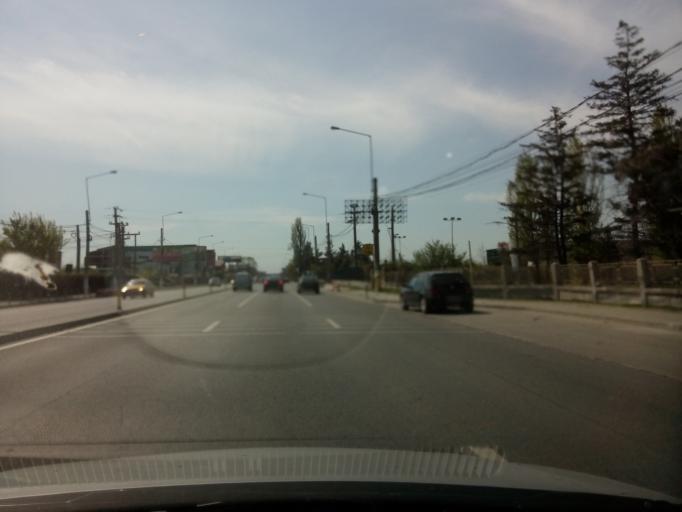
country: RO
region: Ilfov
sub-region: Comuna Otopeni
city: Otopeni
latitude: 44.5599
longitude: 26.0693
